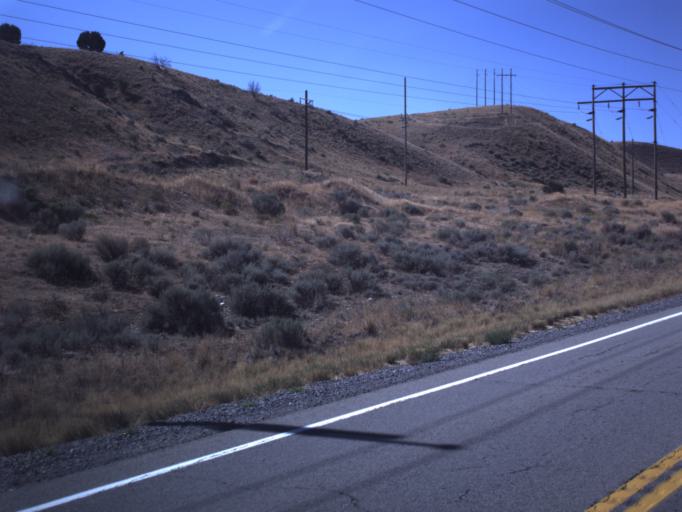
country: US
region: Utah
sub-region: Tooele County
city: Tooele
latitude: 40.4784
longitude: -112.3460
